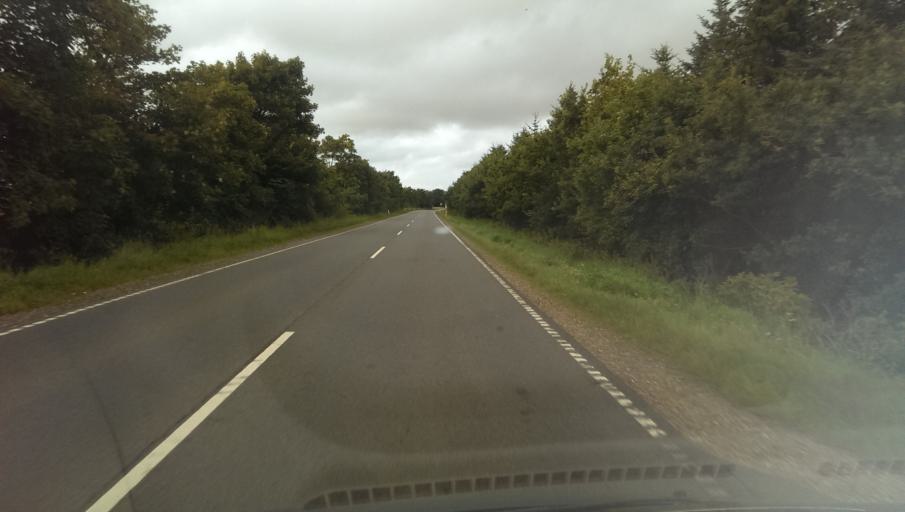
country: DK
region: South Denmark
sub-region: Varde Kommune
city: Olgod
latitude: 55.7054
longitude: 8.6076
